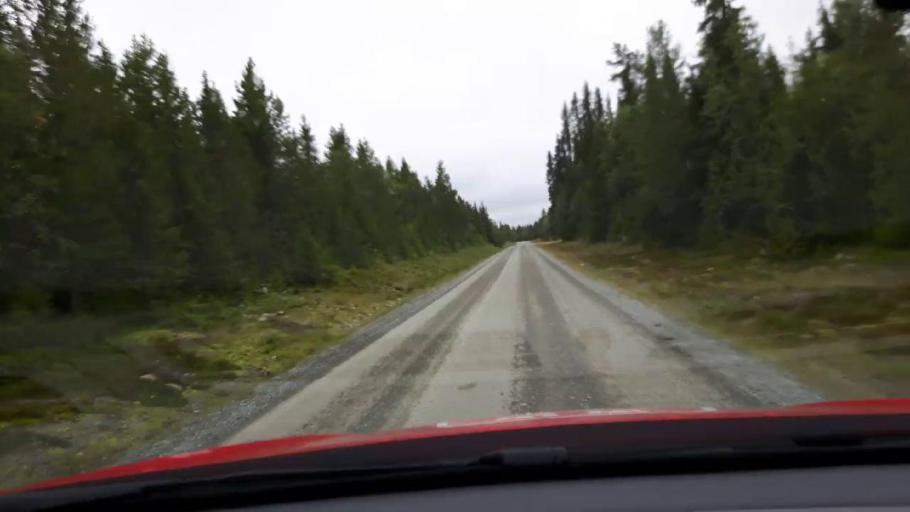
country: SE
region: Jaemtland
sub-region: Bergs Kommun
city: Hoverberg
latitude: 62.8677
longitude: 13.9551
